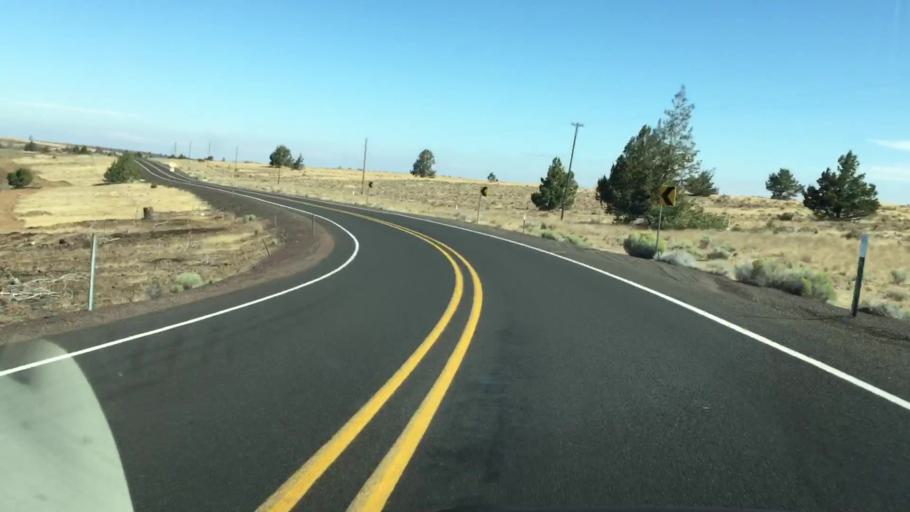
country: US
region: Oregon
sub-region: Jefferson County
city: Warm Springs
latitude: 45.0172
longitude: -120.9896
